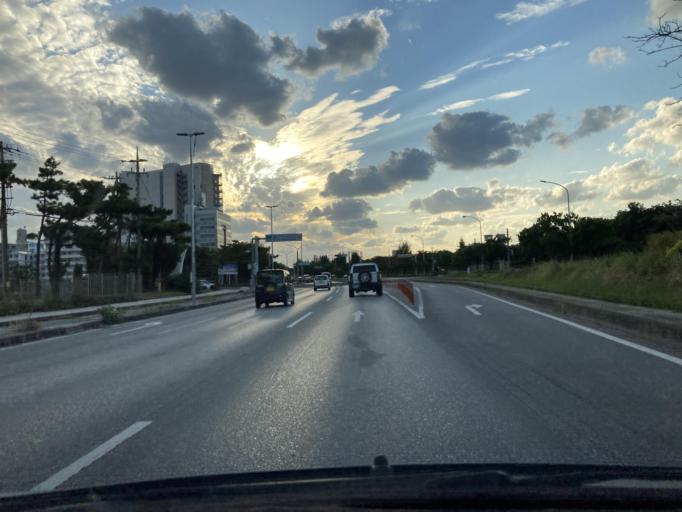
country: JP
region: Okinawa
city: Ginowan
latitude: 26.2789
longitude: 127.7351
